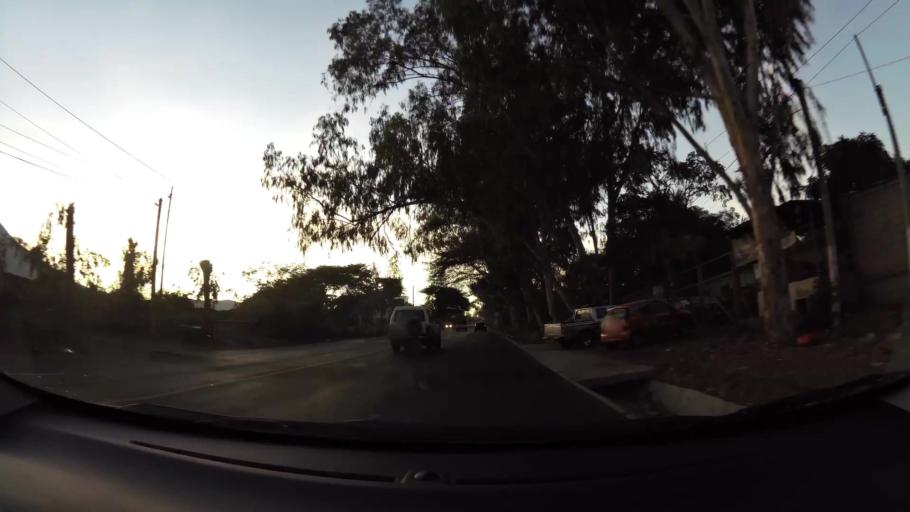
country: SV
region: San Miguel
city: San Miguel
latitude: 13.5004
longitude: -88.2137
